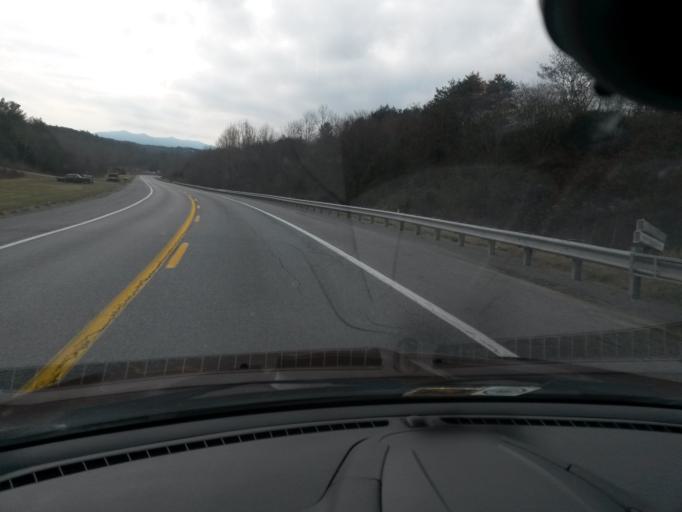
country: US
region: Virginia
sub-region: Alleghany County
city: Clifton Forge
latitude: 37.7588
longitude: -79.7884
